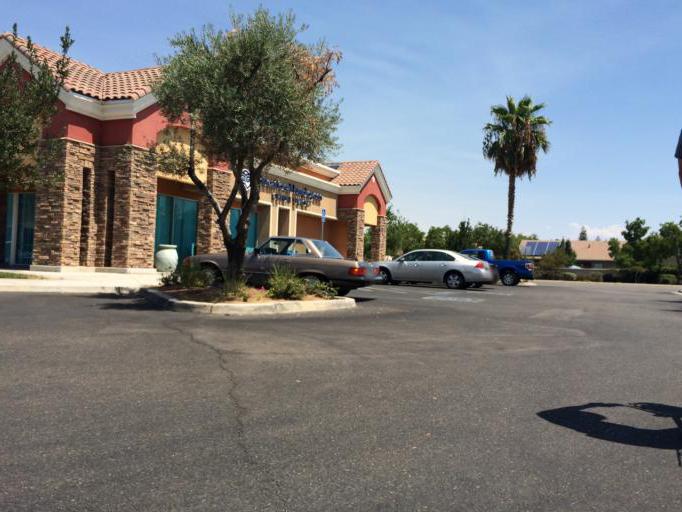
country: US
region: California
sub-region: Fresno County
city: Clovis
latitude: 36.8737
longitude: -119.7411
